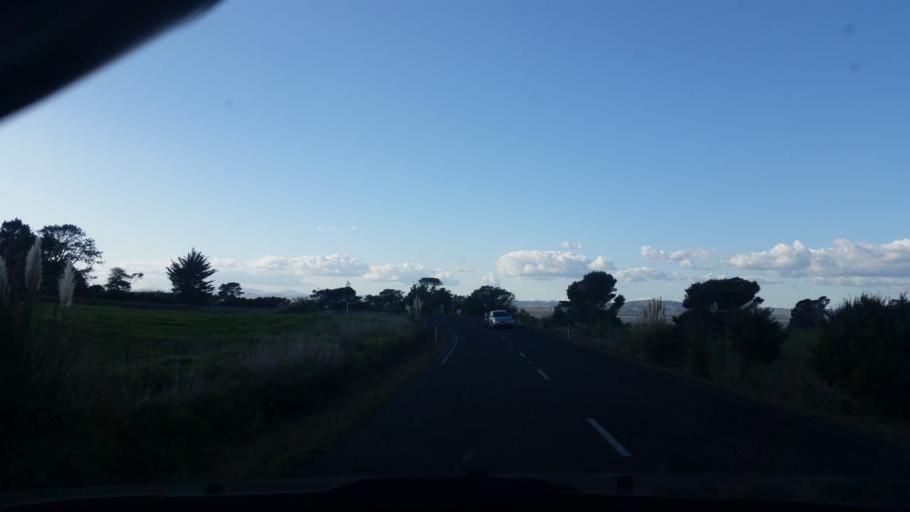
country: NZ
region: Northland
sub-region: Kaipara District
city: Dargaville
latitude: -36.1977
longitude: 174.0509
